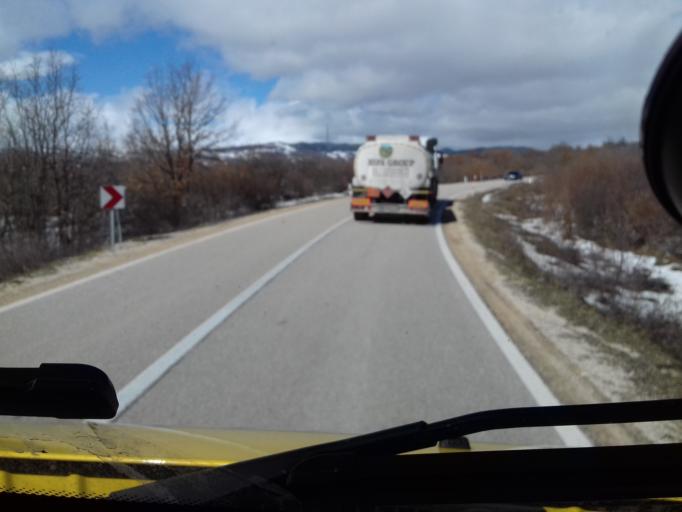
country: BA
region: Federation of Bosnia and Herzegovina
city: Tomislavgrad
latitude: 43.7818
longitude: 17.2226
